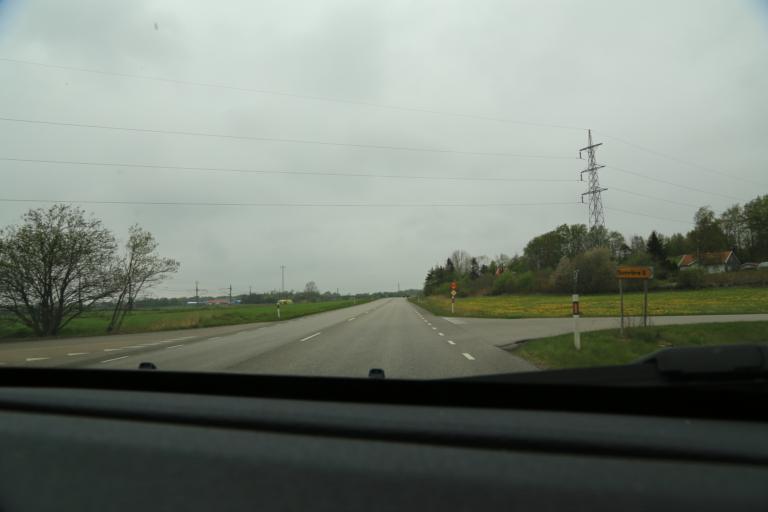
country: SE
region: Halland
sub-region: Kungsbacka Kommun
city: Frillesas
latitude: 57.2358
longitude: 12.2020
